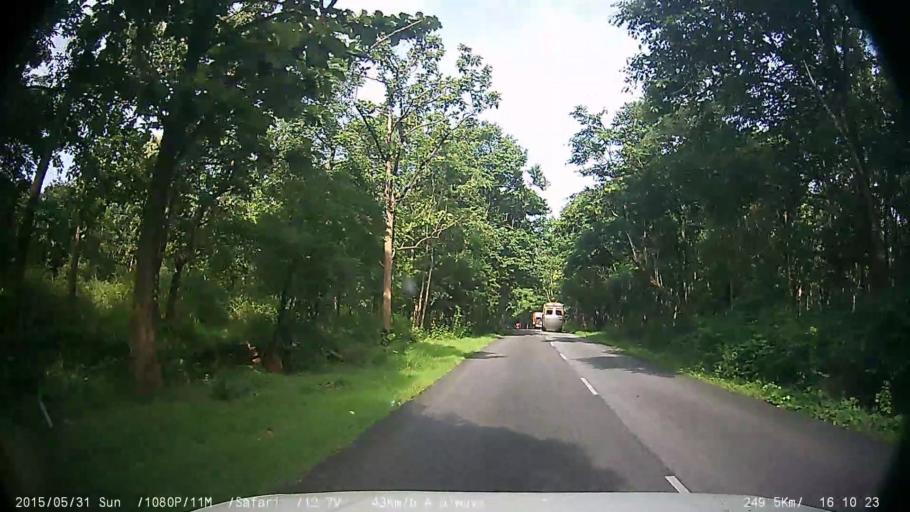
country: IN
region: Karnataka
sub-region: Mysore
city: Sargur
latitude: 11.7305
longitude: 76.4382
